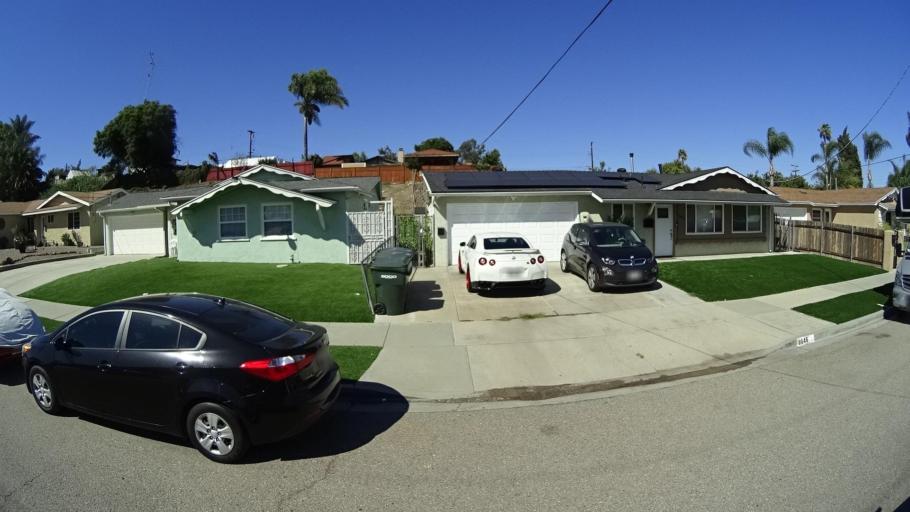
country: US
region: California
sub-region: San Diego County
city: La Presa
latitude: 32.7095
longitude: -117.0171
